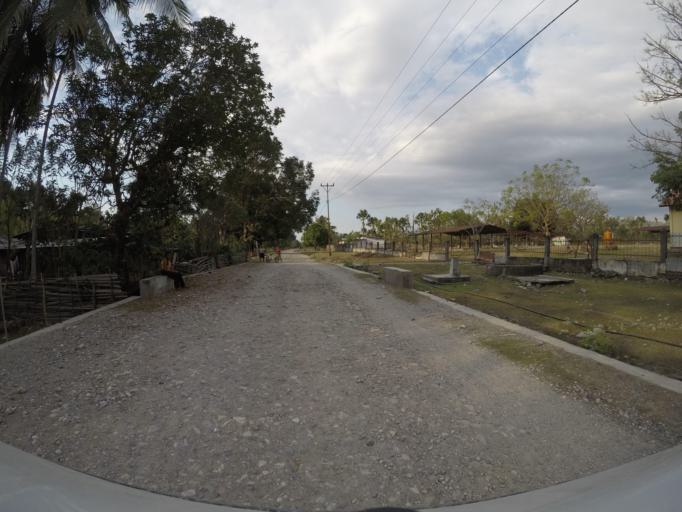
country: TL
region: Bobonaro
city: Maliana
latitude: -8.8707
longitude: 125.2128
